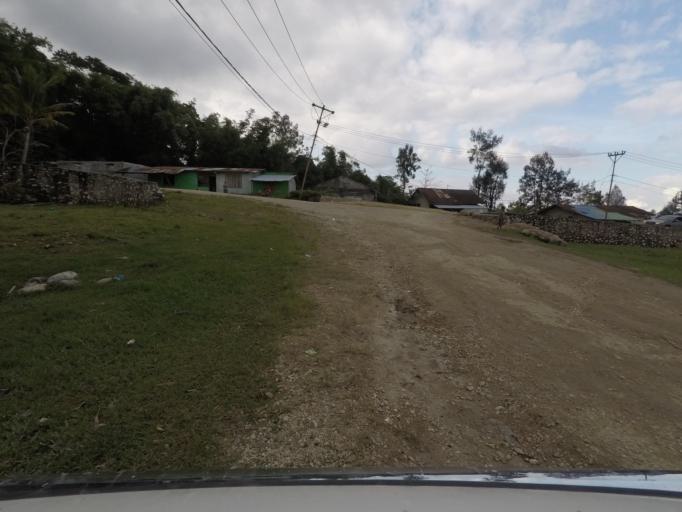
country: TL
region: Baucau
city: Venilale
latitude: -8.7354
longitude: 126.3708
